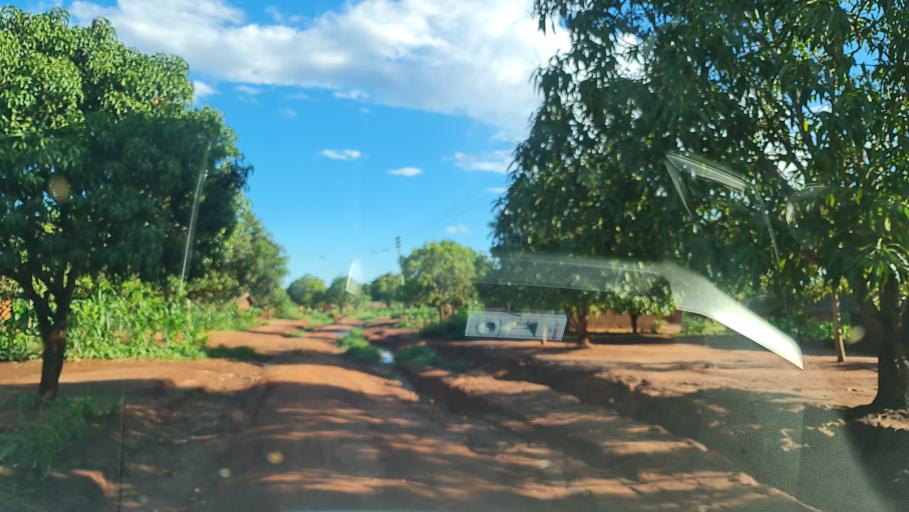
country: MZ
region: Nampula
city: Ilha de Mocambique
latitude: -14.9215
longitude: 40.2181
